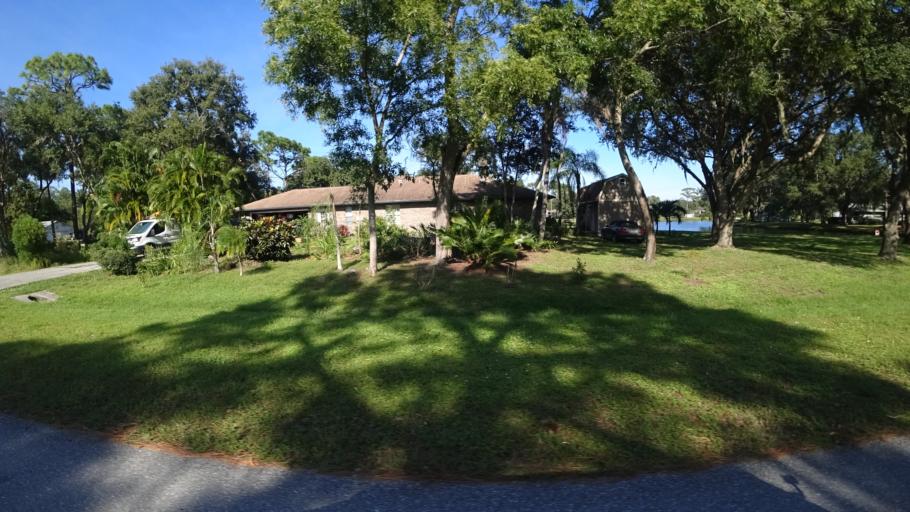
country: US
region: Florida
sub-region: Sarasota County
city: The Meadows
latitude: 27.4228
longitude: -82.4455
